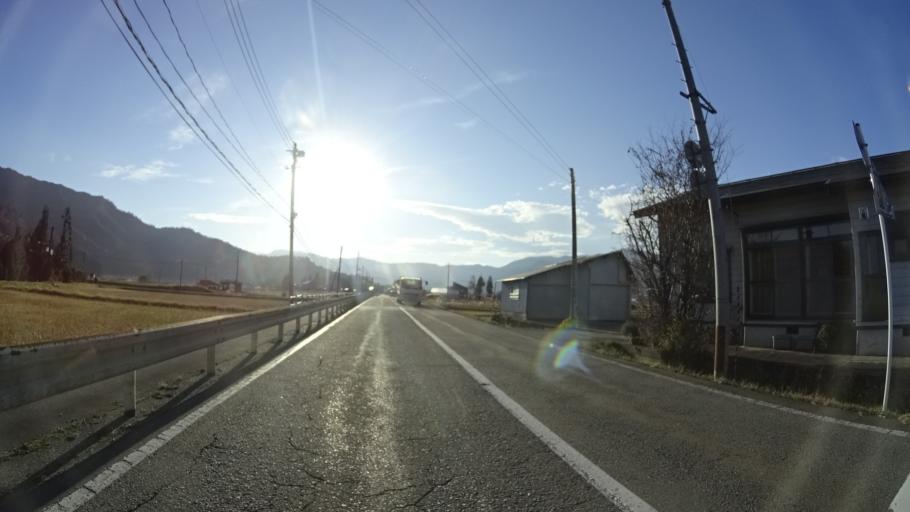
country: JP
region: Niigata
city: Shiozawa
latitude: 37.0112
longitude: 138.8516
